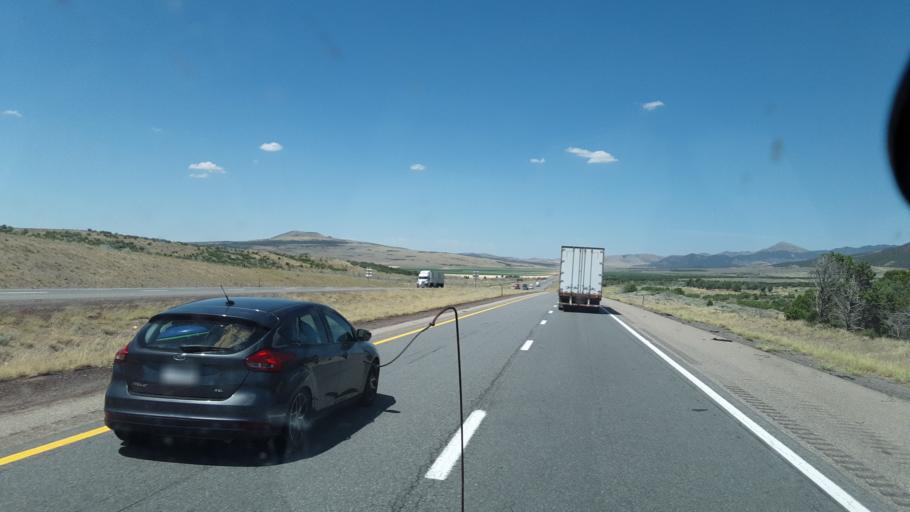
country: US
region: Utah
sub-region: Beaver County
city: Beaver
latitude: 38.4916
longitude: -112.6164
